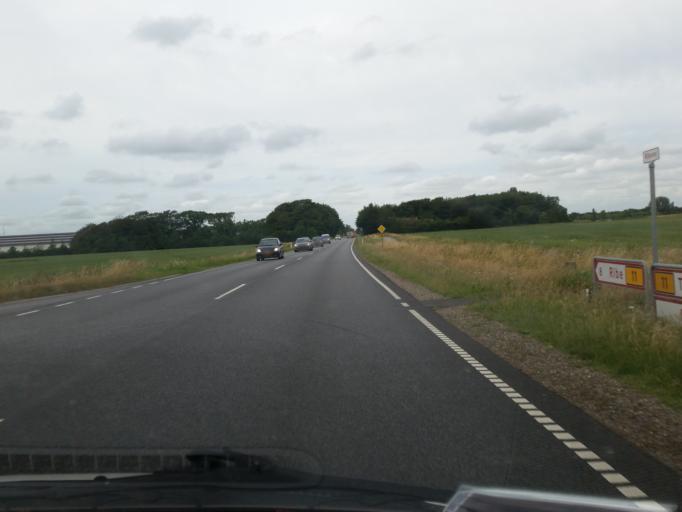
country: DK
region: South Denmark
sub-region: Esbjerg Kommune
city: Ribe
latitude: 55.2641
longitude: 8.7226
